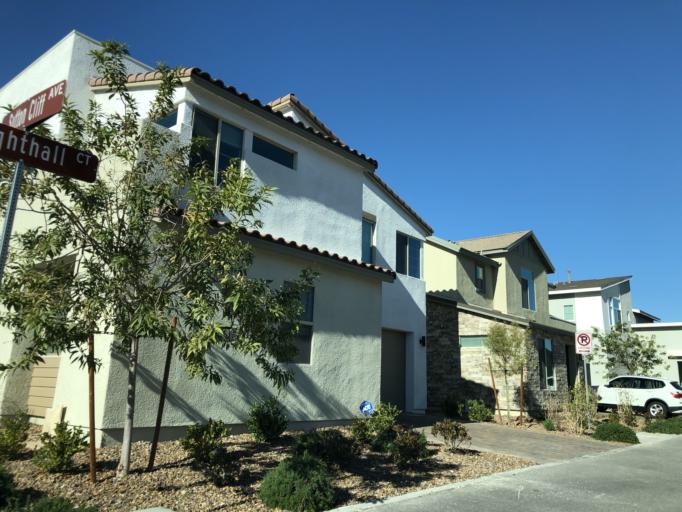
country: US
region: Nevada
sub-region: Clark County
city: Whitney
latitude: 35.9999
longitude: -115.0871
